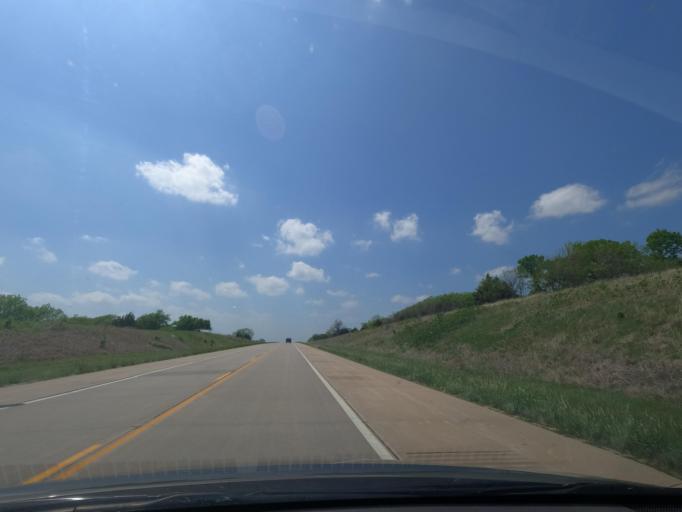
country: US
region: Kansas
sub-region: Wilson County
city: Fredonia
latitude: 37.6231
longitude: -96.0521
